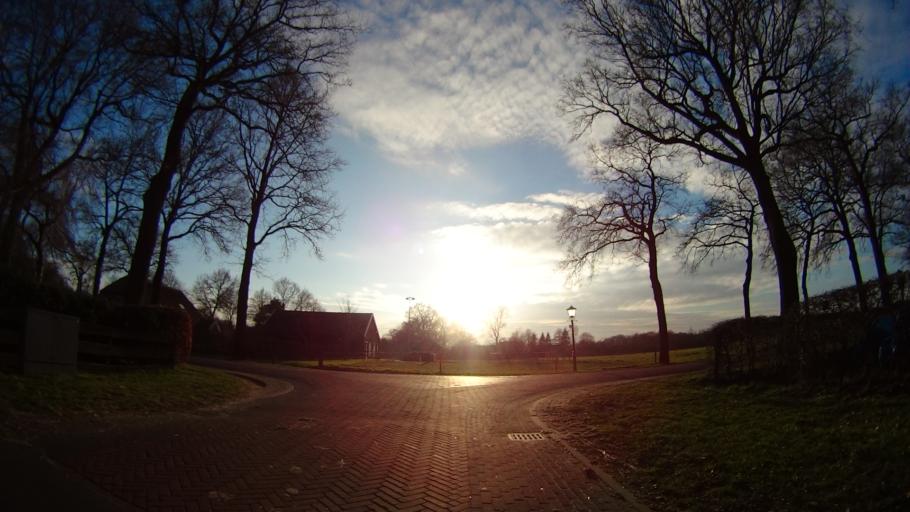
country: NL
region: Drenthe
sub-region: Gemeente Coevorden
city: Sleen
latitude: 52.8127
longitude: 6.7187
